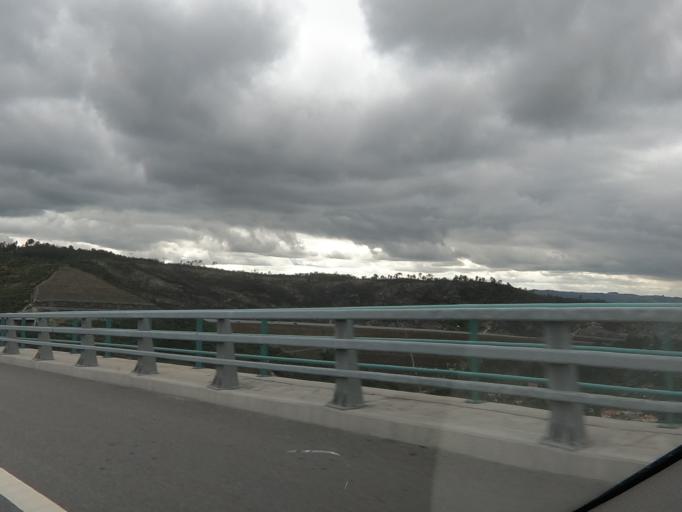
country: PT
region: Porto
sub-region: Amarante
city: Amarante
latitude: 41.2498
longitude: -7.9854
